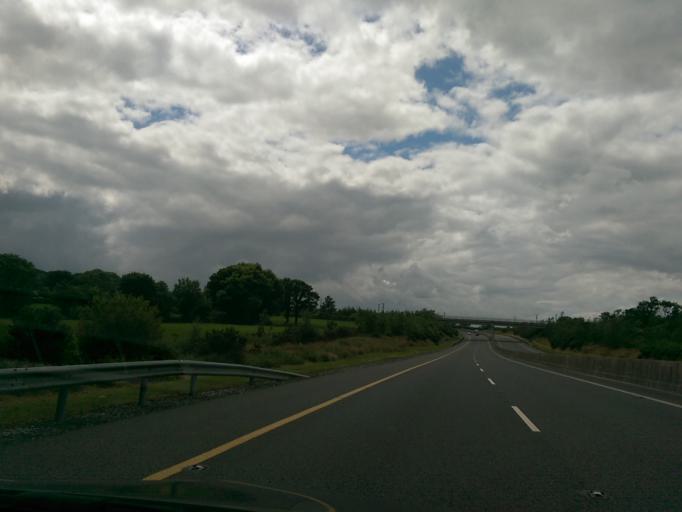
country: IE
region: Munster
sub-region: County Cork
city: Mitchelstown
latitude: 52.2492
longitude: -8.2630
